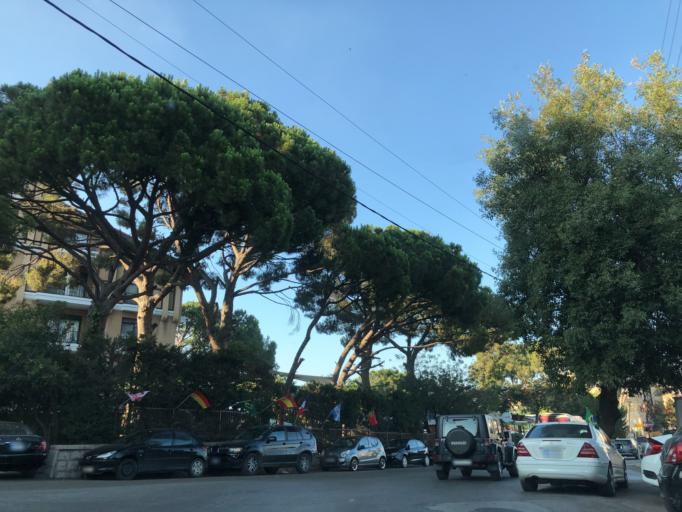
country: LB
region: Mont-Liban
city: Jdaidet el Matn
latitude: 33.8843
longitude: 35.6362
